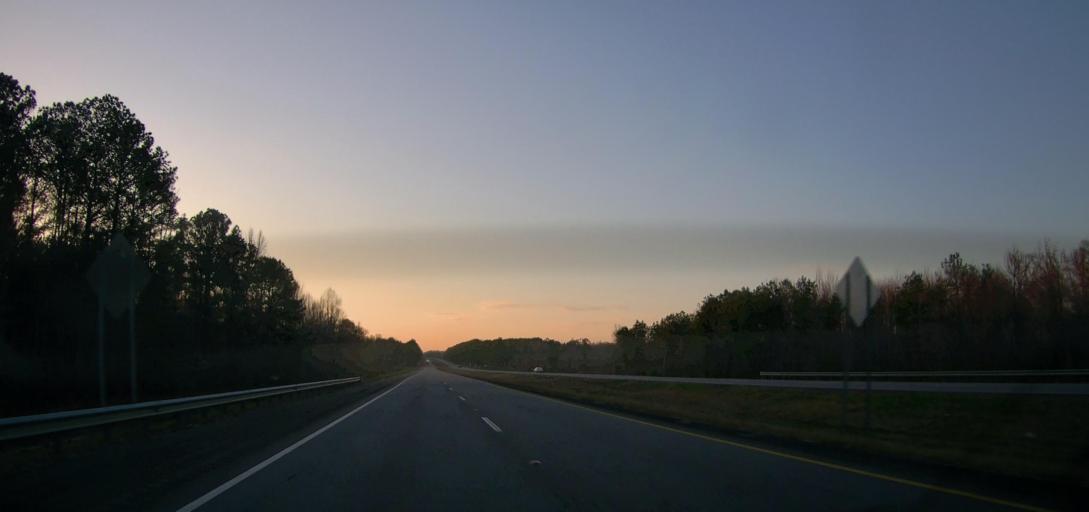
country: US
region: Alabama
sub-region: Coosa County
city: Goodwater
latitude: 33.0009
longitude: -86.0826
